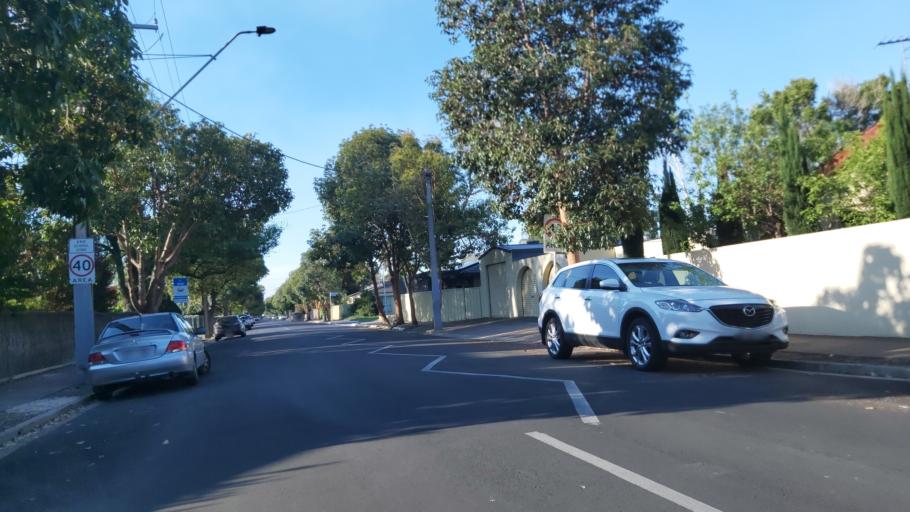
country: AU
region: South Australia
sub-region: Unley
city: Fullarton
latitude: -34.9539
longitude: 138.6218
